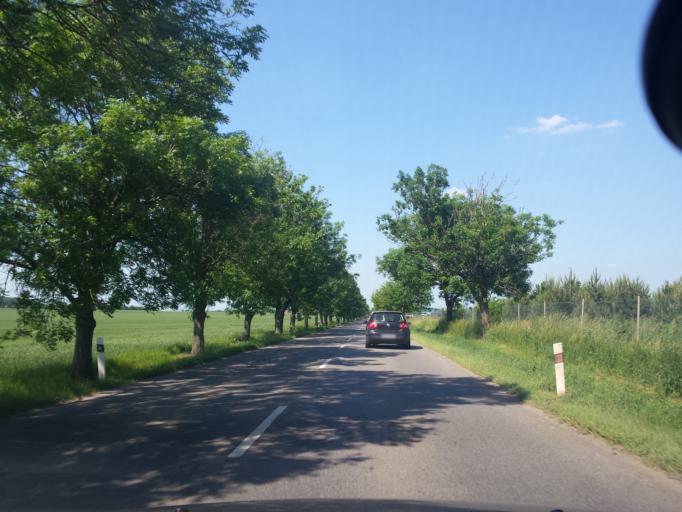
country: CZ
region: Central Bohemia
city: Velke Prilepy
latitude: 50.1730
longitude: 14.3177
